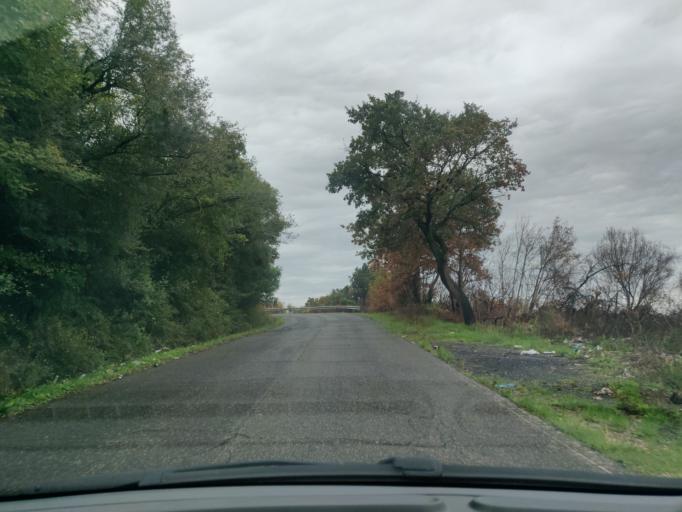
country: IT
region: Latium
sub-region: Citta metropolitana di Roma Capitale
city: Allumiere
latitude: 42.1272
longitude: 11.8556
